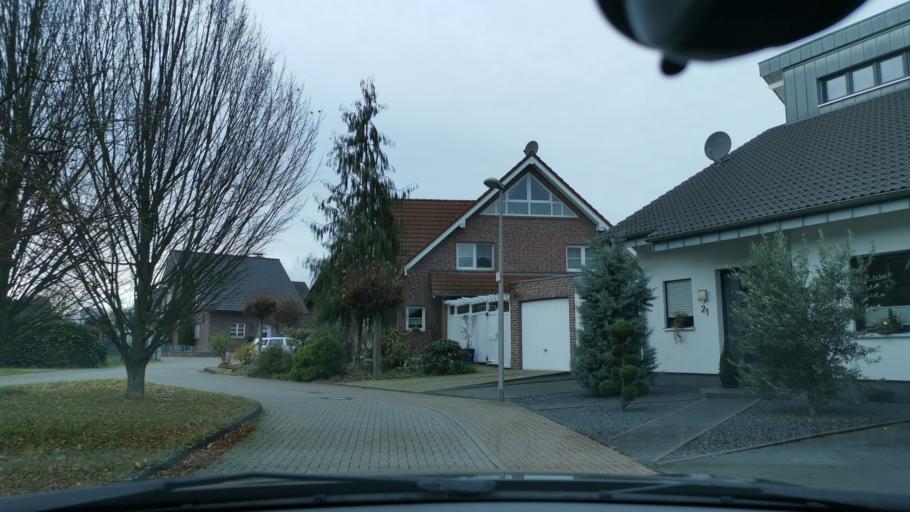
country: DE
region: North Rhine-Westphalia
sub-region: Regierungsbezirk Dusseldorf
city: Rommerskirchen
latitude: 51.0331
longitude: 6.6797
